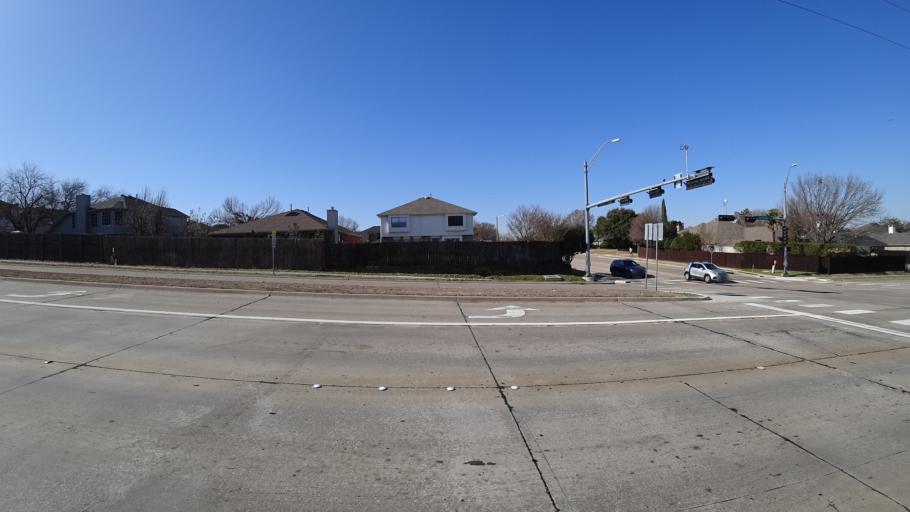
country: US
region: Texas
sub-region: Denton County
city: Lewisville
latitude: 33.0100
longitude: -97.0047
